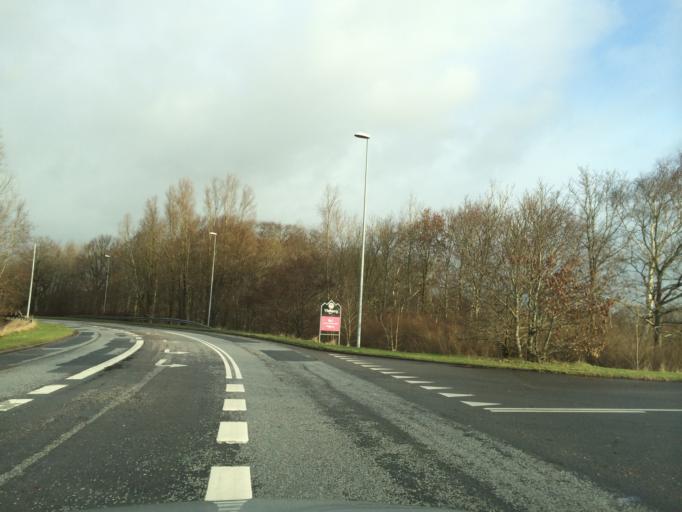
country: DK
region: Central Jutland
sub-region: Herning Kommune
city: Vildbjerg
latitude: 56.1857
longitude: 8.7668
